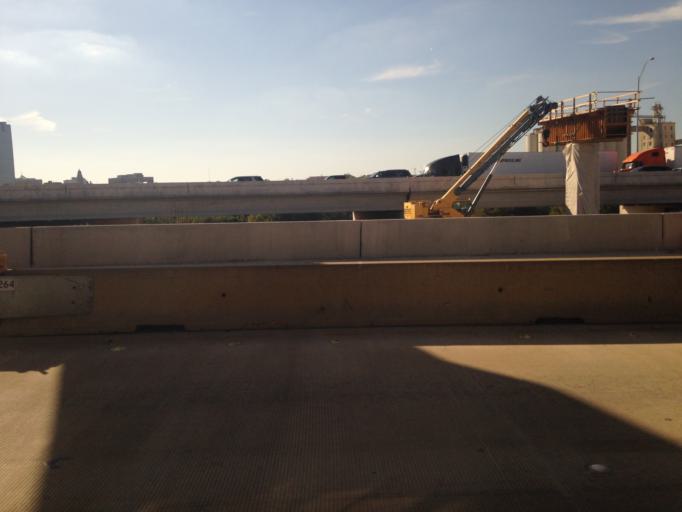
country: US
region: Texas
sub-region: Tarrant County
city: Fort Worth
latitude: 32.7583
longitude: -97.3184
